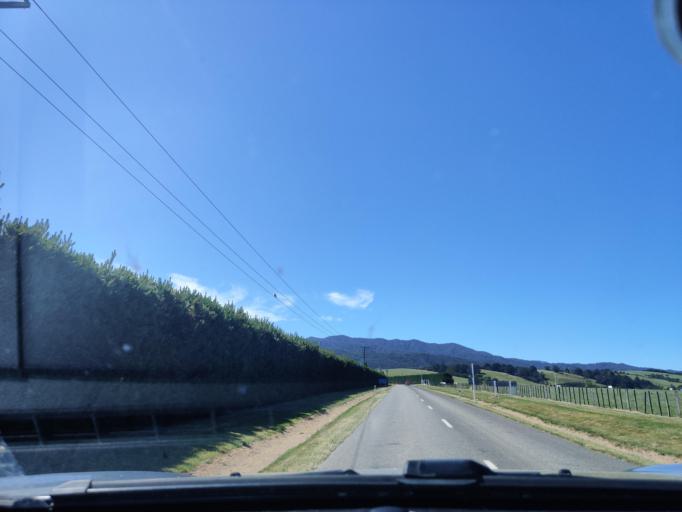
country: NZ
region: Wellington
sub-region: South Wairarapa District
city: Waipawa
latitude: -41.3034
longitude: 175.2718
